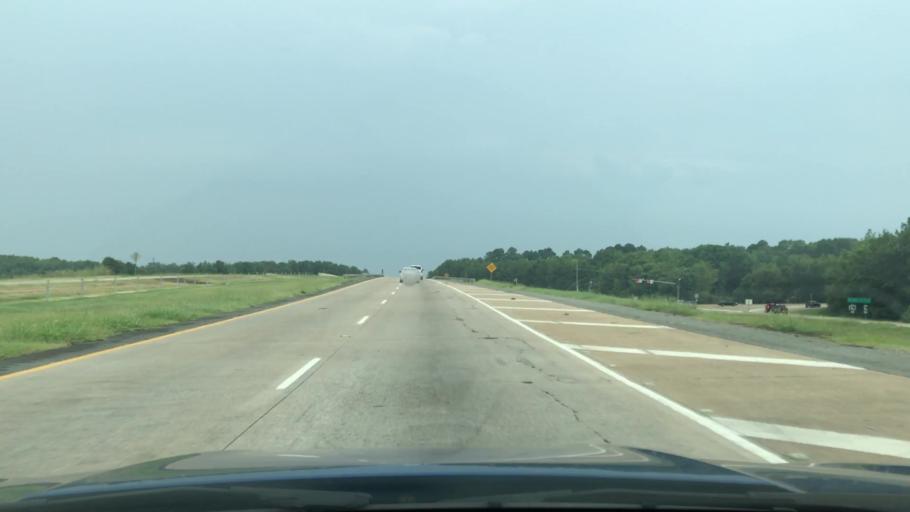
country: US
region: Louisiana
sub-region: Caddo Parish
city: Shreveport
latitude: 32.4443
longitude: -93.8426
